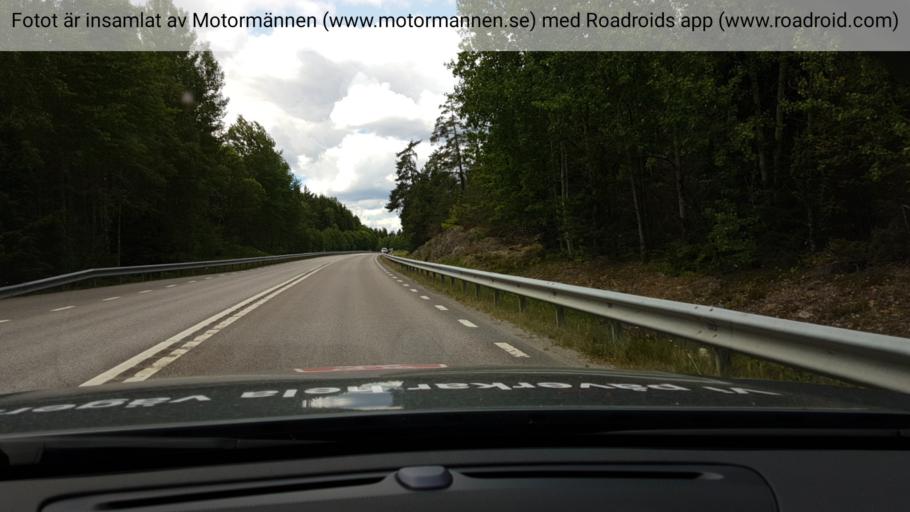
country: SE
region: Stockholm
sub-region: Osterakers Kommun
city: Akersberga
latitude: 59.4270
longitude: 18.2450
